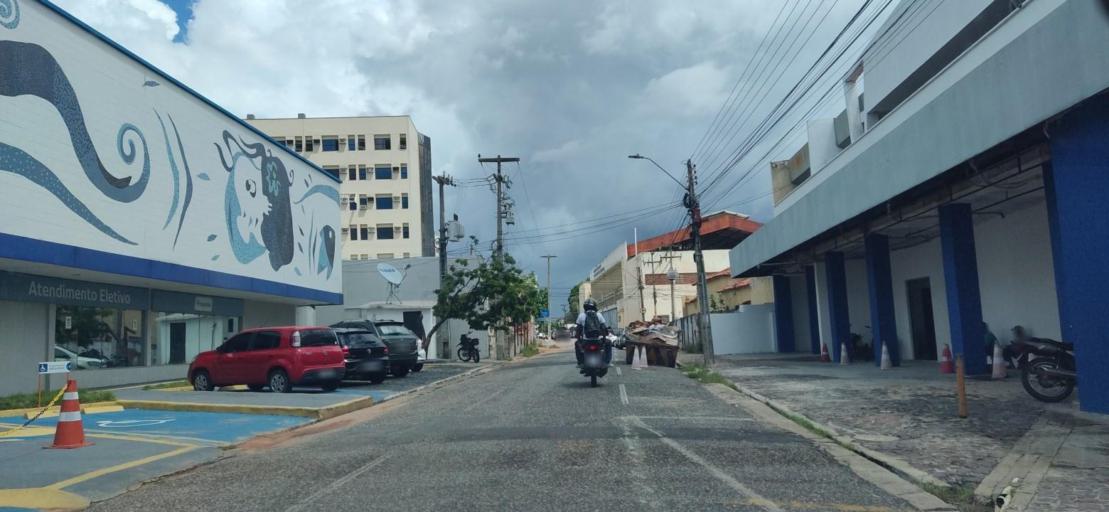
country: BR
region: Piaui
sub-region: Teresina
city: Teresina
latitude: -5.0876
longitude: -42.8113
